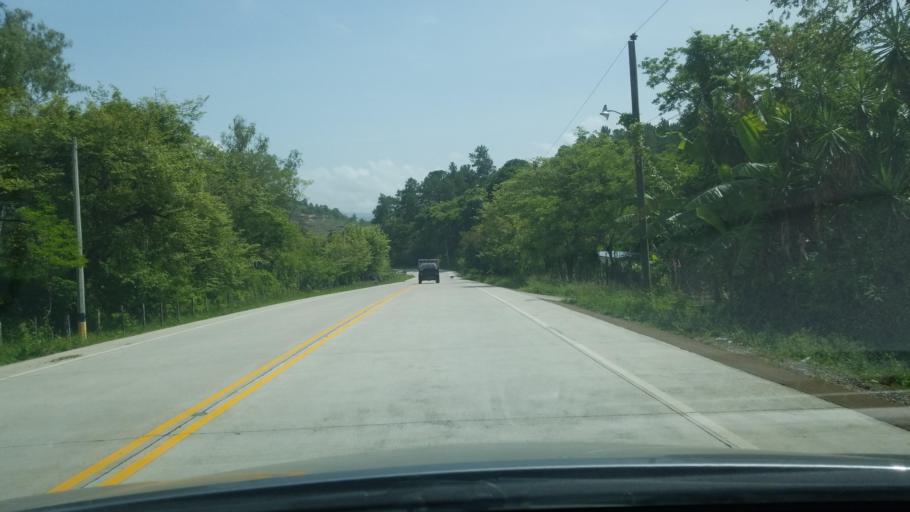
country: HN
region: Copan
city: Florida
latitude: 15.0070
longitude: -88.8360
